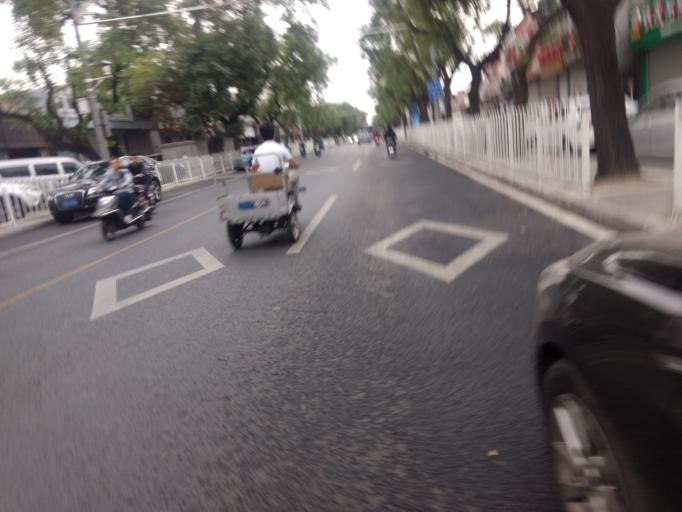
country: CN
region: Beijing
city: Jinrongjie
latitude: 39.9366
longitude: 116.3666
